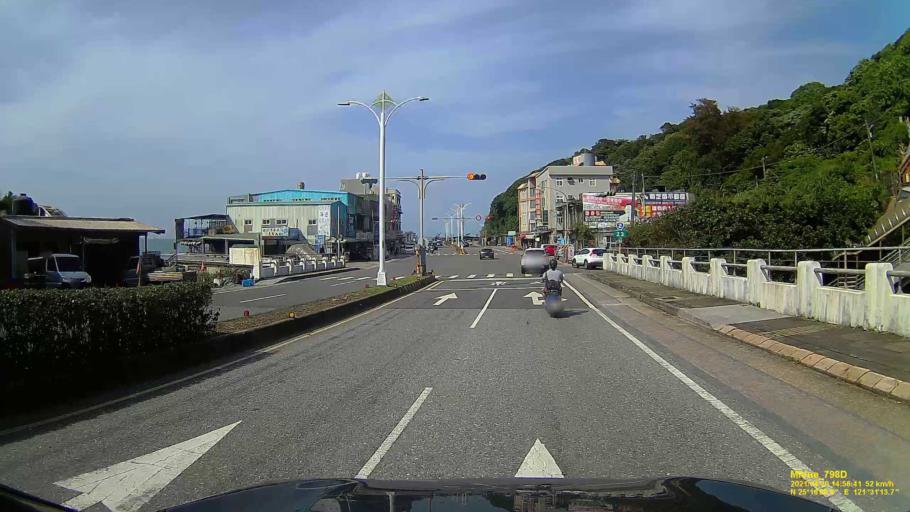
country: TW
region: Taipei
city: Taipei
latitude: 25.2832
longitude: 121.5207
